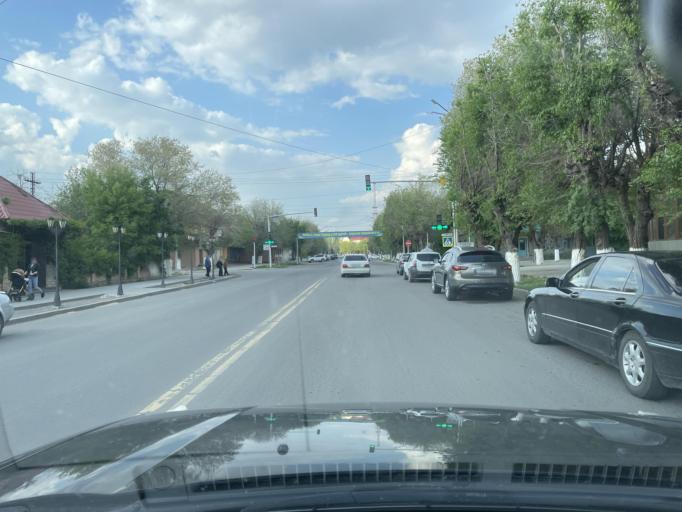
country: KZ
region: Qaraghandy
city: Zhezqazghan
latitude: 47.7910
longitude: 67.7113
